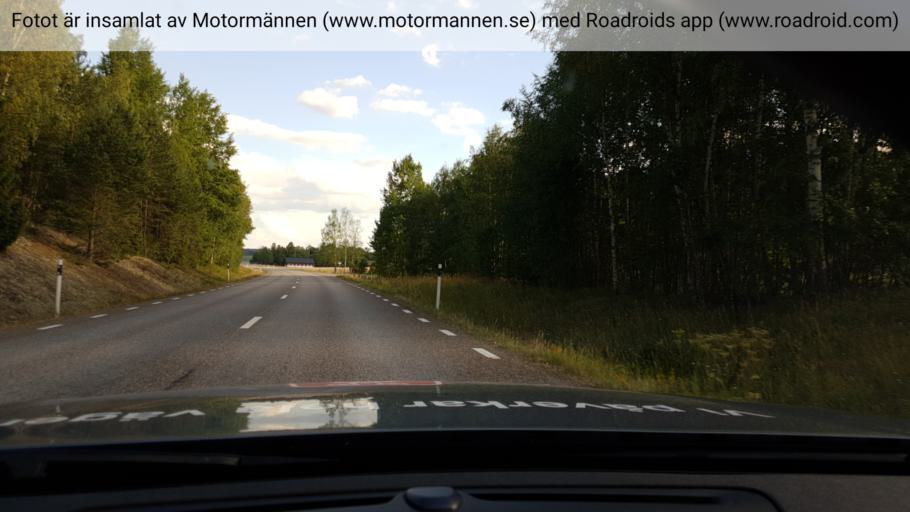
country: SE
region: Uppsala
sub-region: Heby Kommun
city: Morgongava
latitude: 59.8443
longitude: 16.9253
